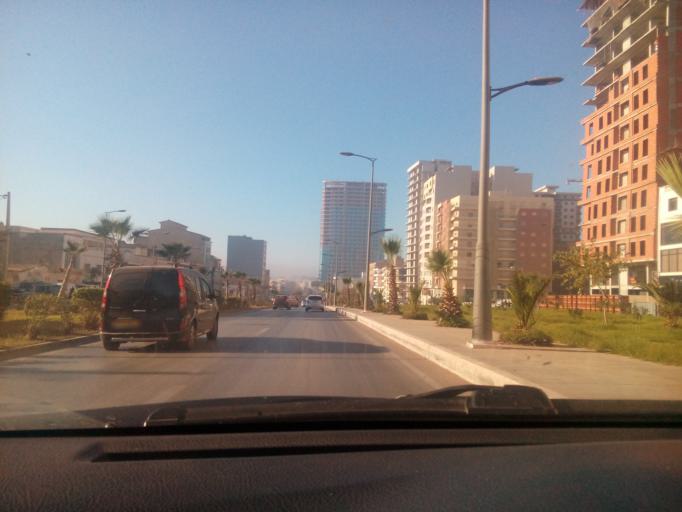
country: DZ
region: Oran
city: Bir el Djir
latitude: 35.7313
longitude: -0.5829
